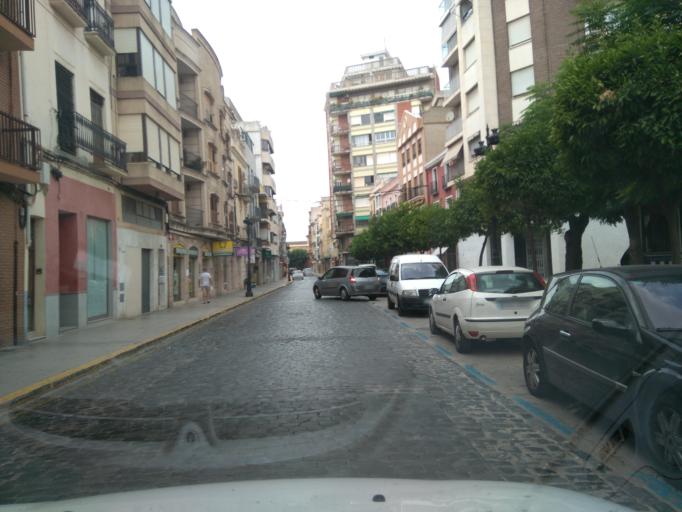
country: ES
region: Valencia
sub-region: Provincia de Valencia
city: Carcaixent
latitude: 39.1207
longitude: -0.4476
